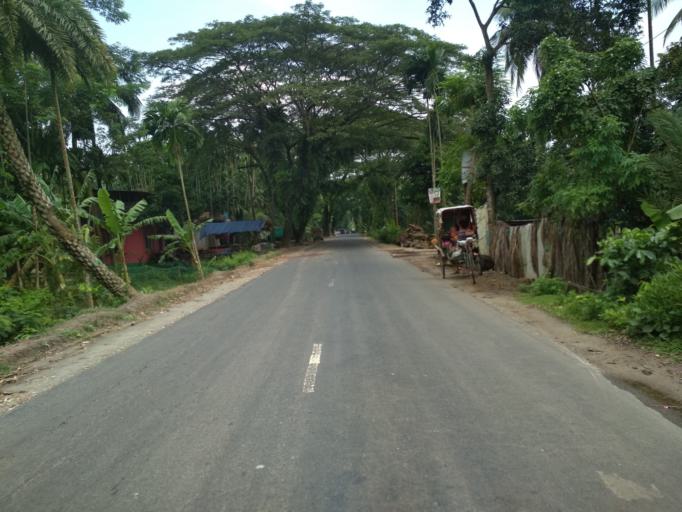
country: BD
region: Chittagong
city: Lakshmipur
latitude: 22.9616
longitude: 90.8096
